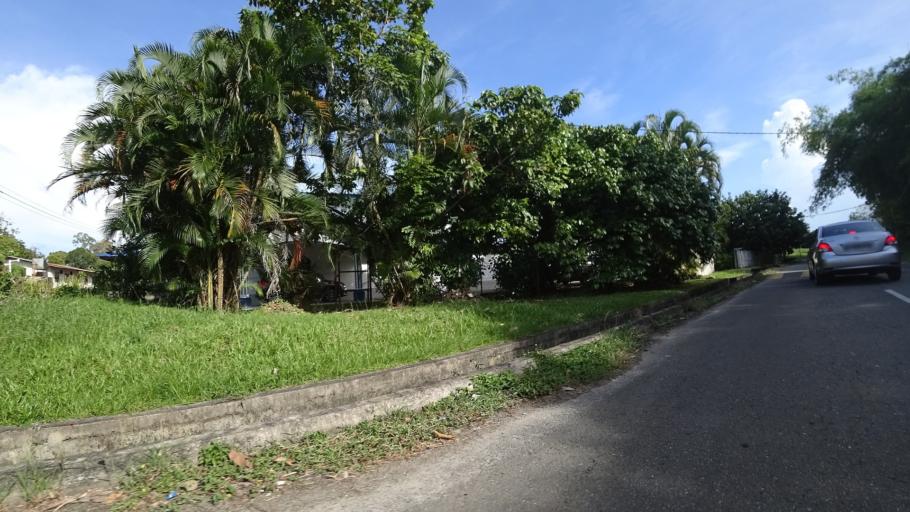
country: BN
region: Brunei and Muara
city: Bandar Seri Begawan
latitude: 4.9331
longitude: 114.8435
